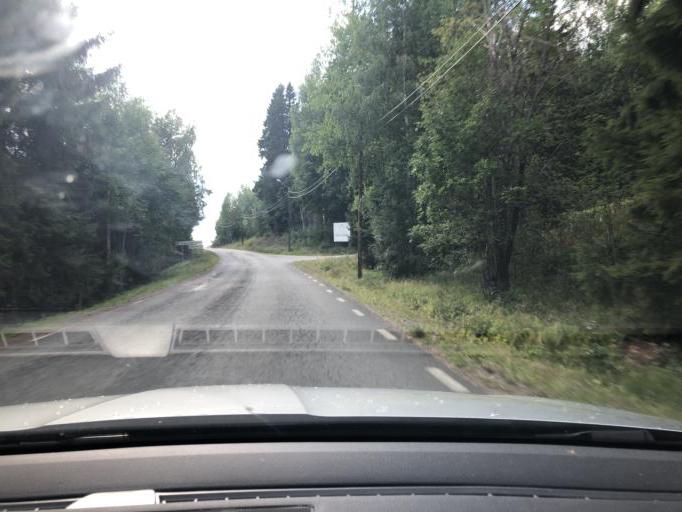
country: SE
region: Vaesternorrland
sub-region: Solleftea Kommun
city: Solleftea
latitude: 63.2108
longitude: 17.1726
